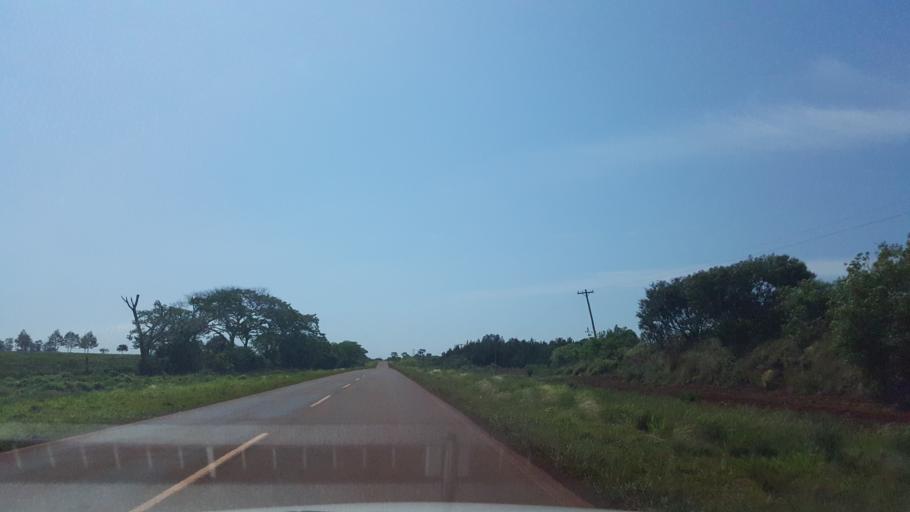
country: AR
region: Corrientes
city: San Carlos
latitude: -27.7513
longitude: -55.8800
